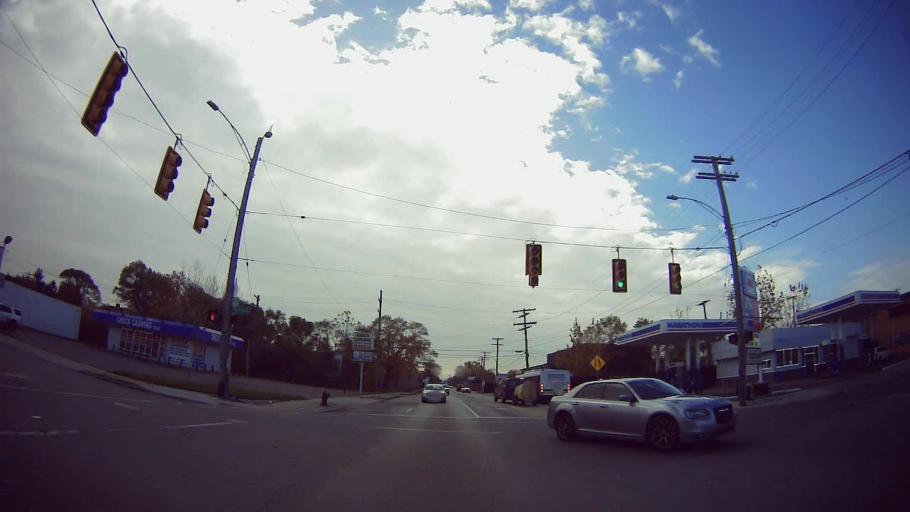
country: US
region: Michigan
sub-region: Wayne County
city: Dearborn
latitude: 42.3731
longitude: -83.1780
